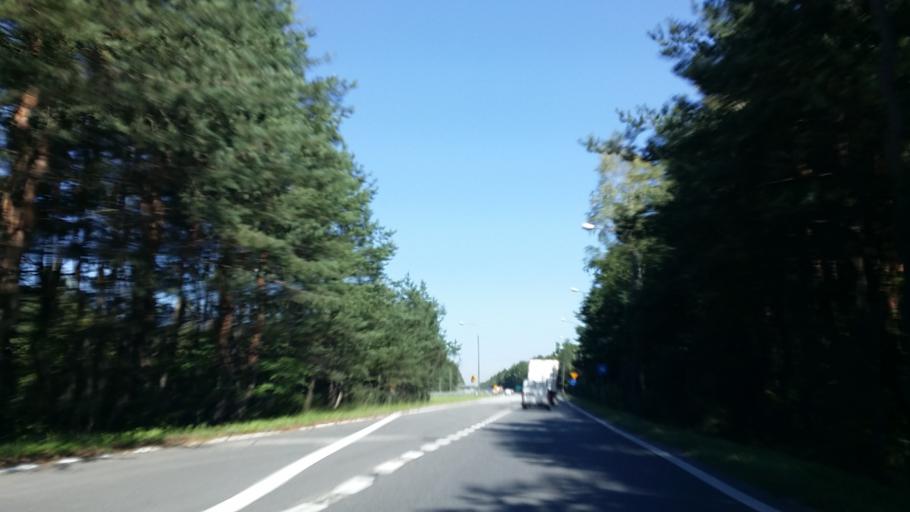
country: PL
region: Silesian Voivodeship
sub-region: Powiat bierunsko-ledzinski
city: Imielin
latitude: 50.1714
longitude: 19.1698
